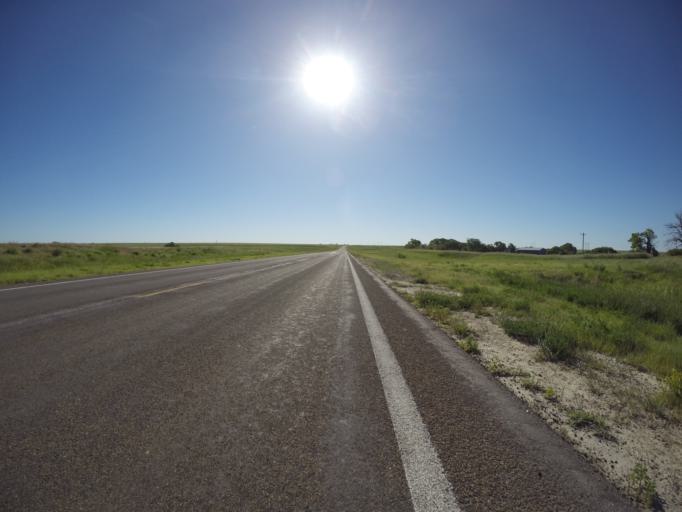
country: US
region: Kansas
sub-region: Norton County
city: Norton
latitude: 39.8280
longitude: -100.0264
